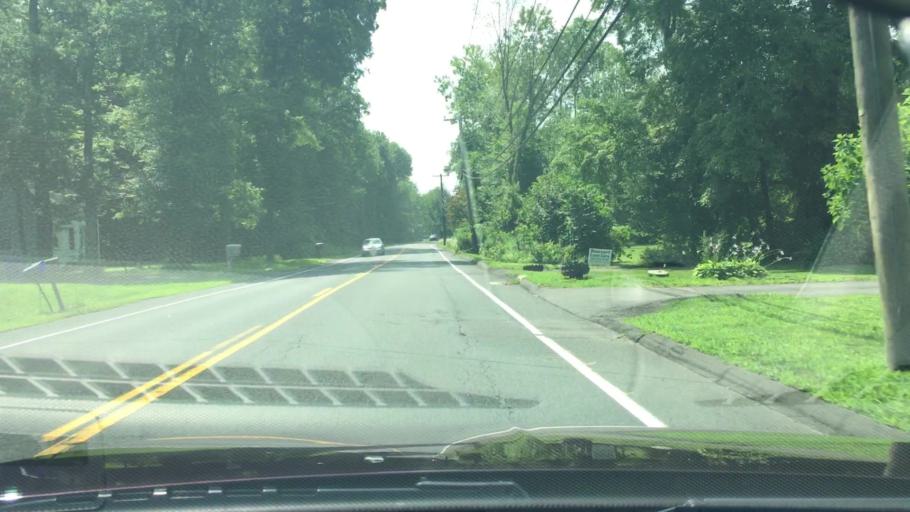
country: US
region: Connecticut
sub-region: Hartford County
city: Blue Hills
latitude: 41.8491
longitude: -72.7014
